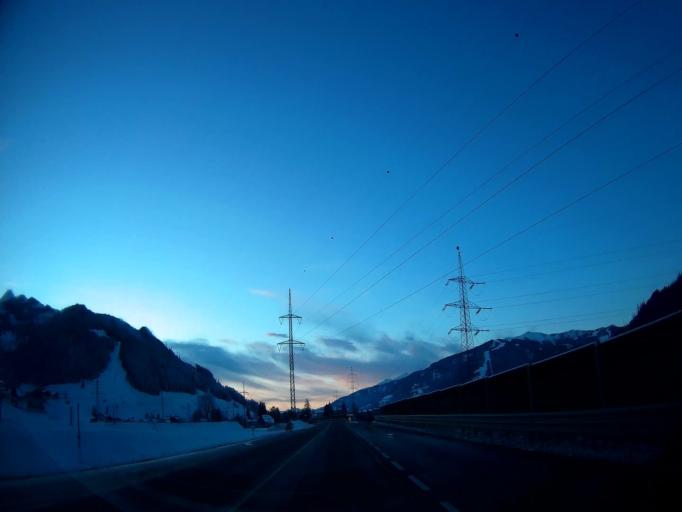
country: AT
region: Salzburg
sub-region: Politischer Bezirk Zell am See
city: Bruck an der Grossglocknerstrasse
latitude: 47.2787
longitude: 12.8381
